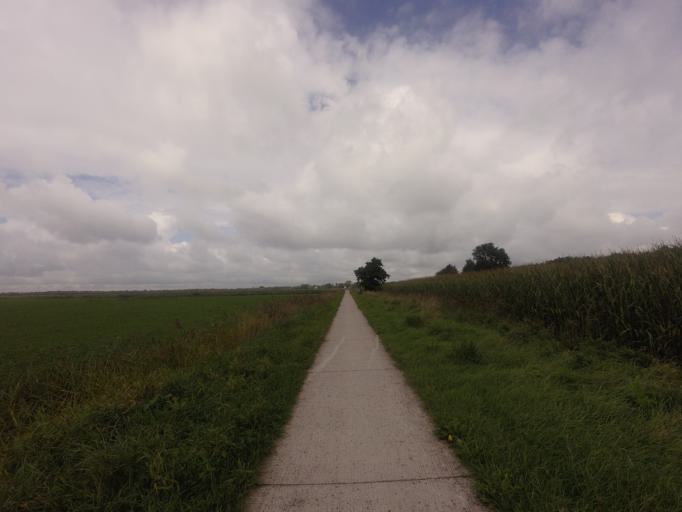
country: NL
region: Friesland
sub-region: Gemeente Skarsterlan
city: Oudehaske
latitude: 52.9437
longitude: 5.8504
